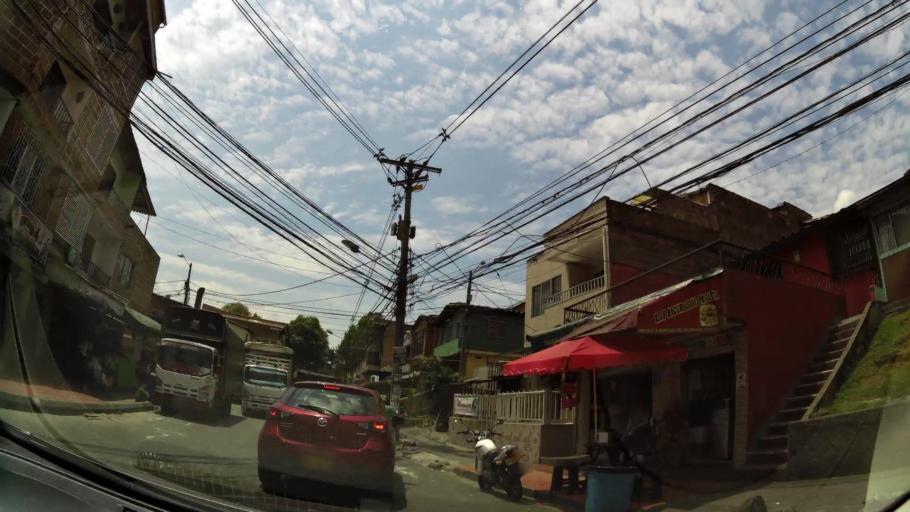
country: CO
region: Antioquia
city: Bello
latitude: 6.3121
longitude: -75.5700
